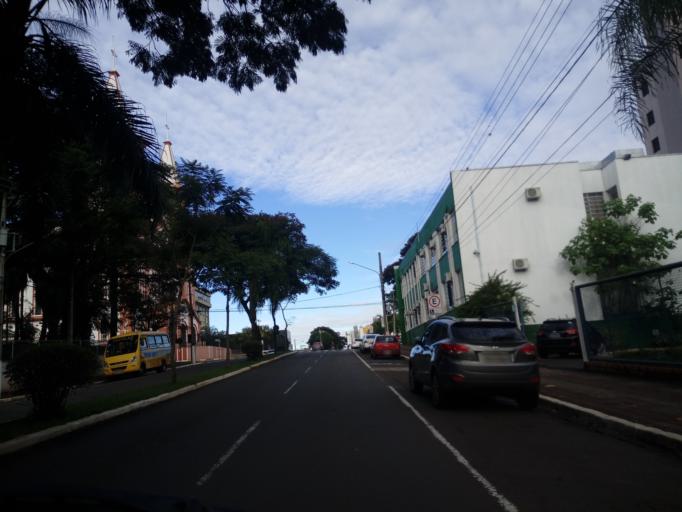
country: BR
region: Santa Catarina
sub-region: Chapeco
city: Chapeco
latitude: -27.1044
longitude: -52.6128
